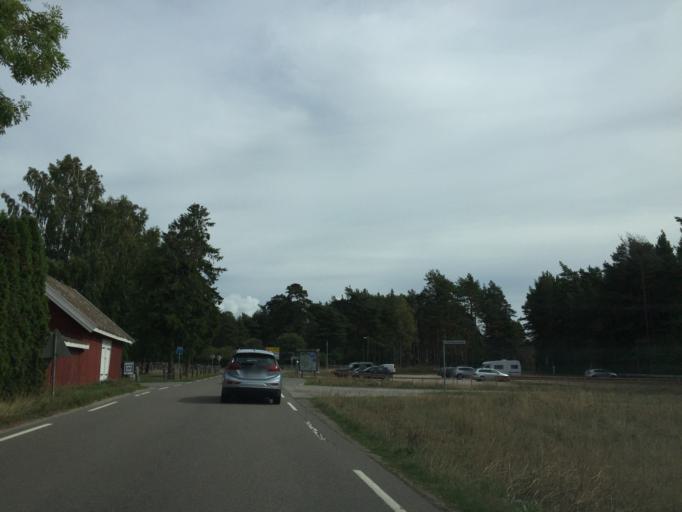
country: NO
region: Ostfold
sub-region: Hvaler
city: Skjaerhalden
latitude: 59.0319
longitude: 11.0231
